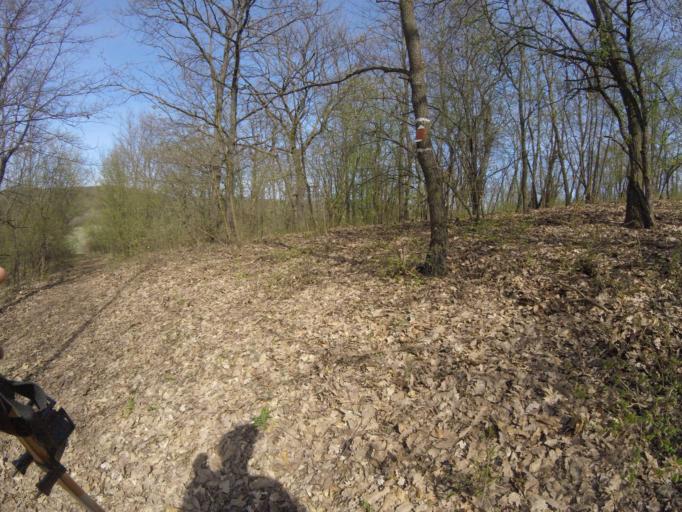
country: HU
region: Borsod-Abauj-Zemplen
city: Szendro
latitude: 48.4253
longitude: 20.7549
